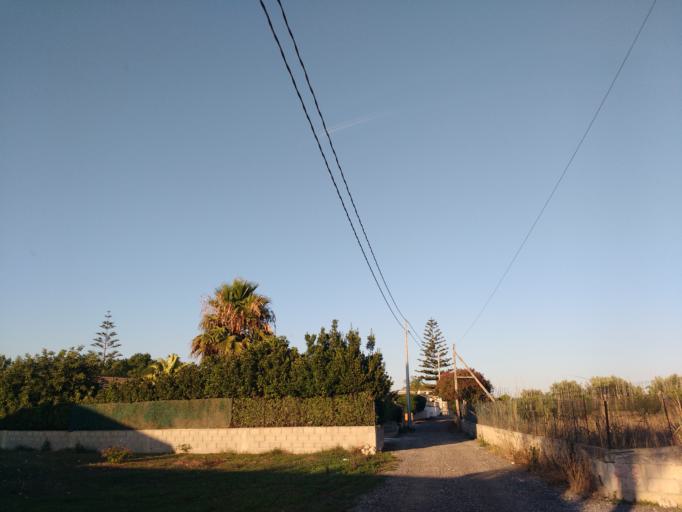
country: IT
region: Sicily
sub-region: Ragusa
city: Ispica
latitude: 36.7282
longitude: 14.9193
